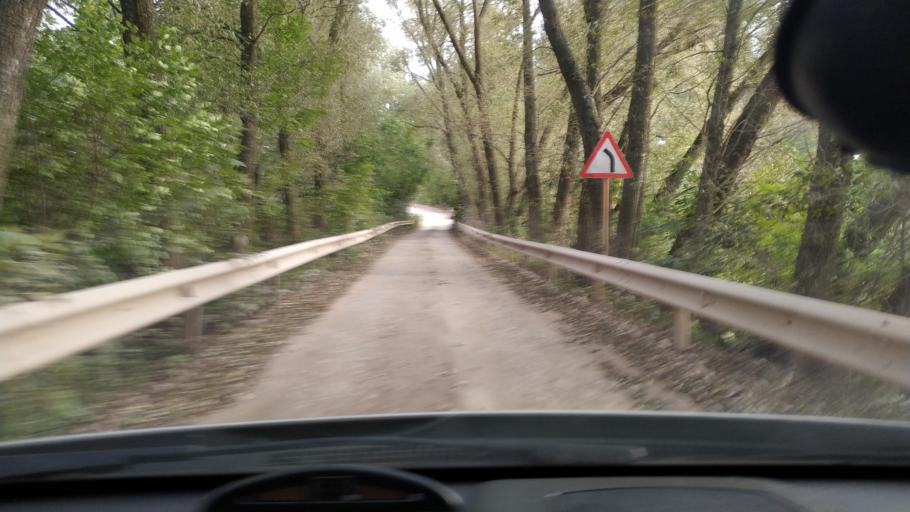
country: RU
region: Rjazan
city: Polyany
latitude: 54.5622
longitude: 39.8750
